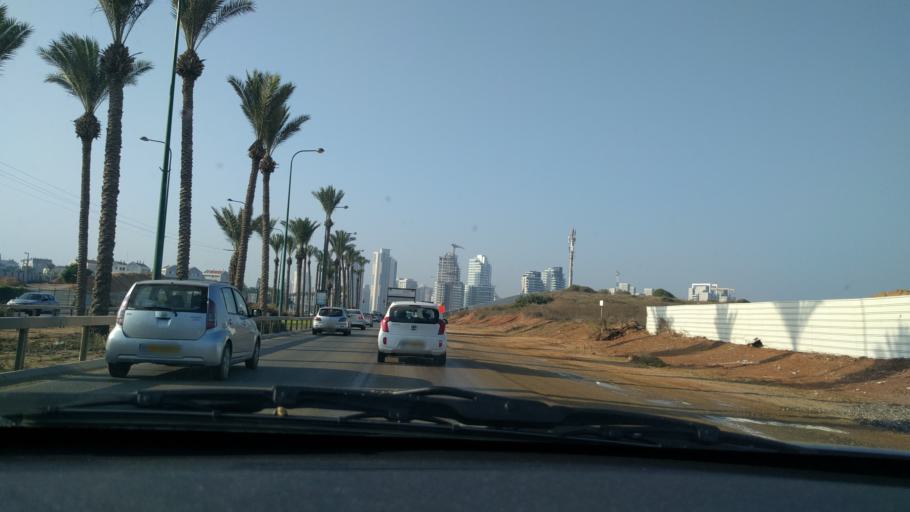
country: IL
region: Central District
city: Netanya
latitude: 32.2898
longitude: 34.8425
